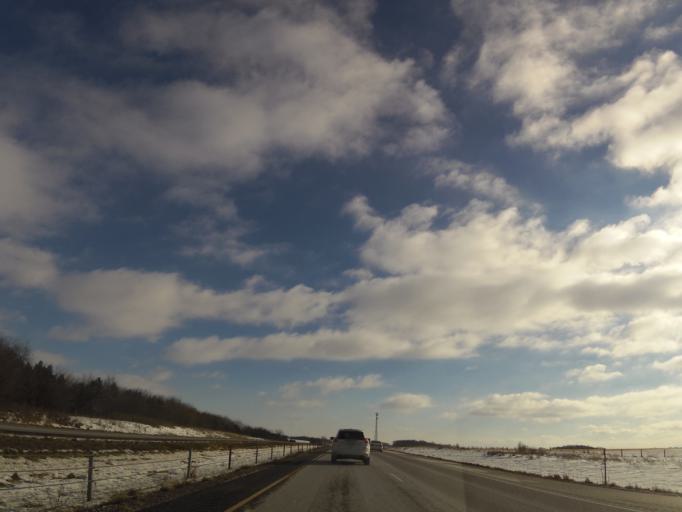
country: US
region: Wisconsin
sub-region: Dunn County
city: Colfax
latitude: 44.8632
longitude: -91.6794
